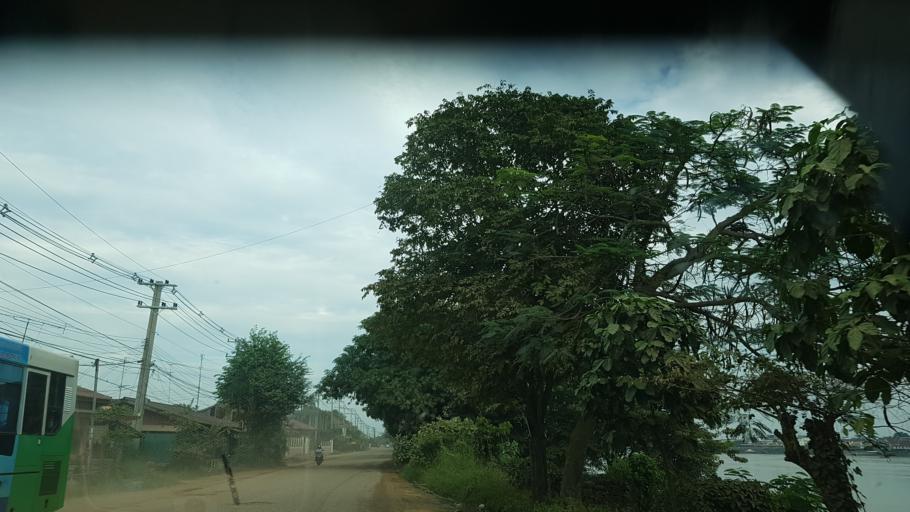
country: TH
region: Nong Khai
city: Nong Khai
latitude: 17.8880
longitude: 102.7338
